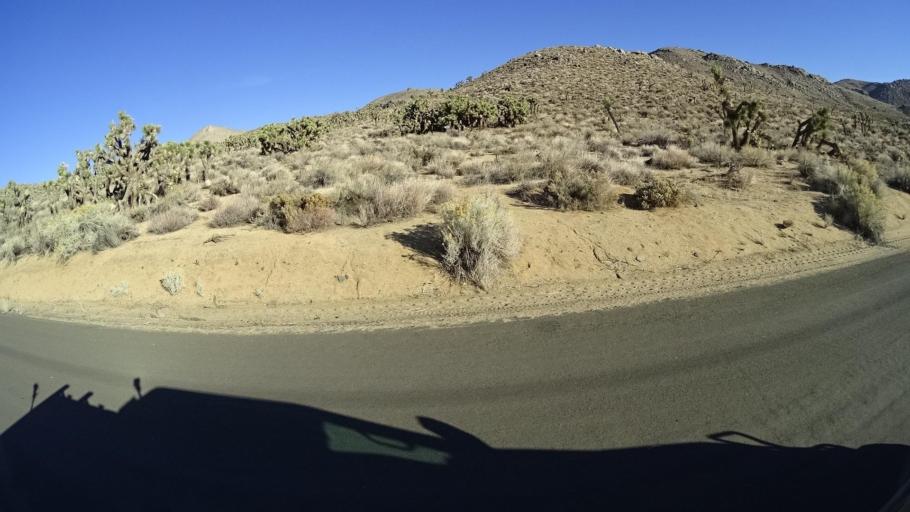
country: US
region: California
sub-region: Kern County
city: Weldon
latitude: 35.5193
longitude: -118.2037
